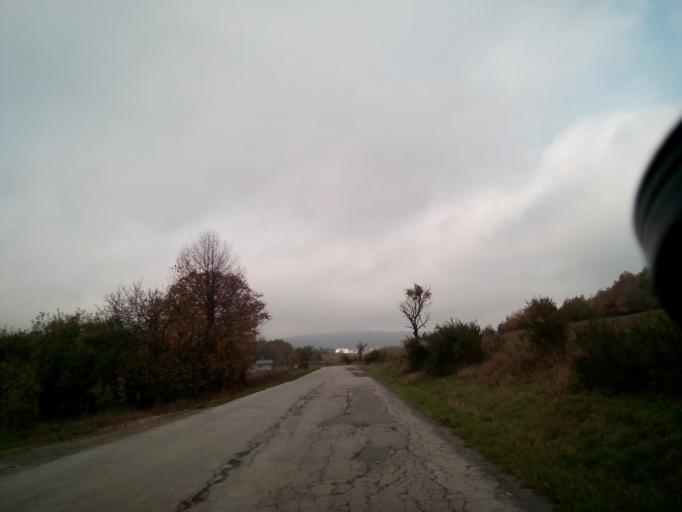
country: SK
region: Kosicky
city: Kosice
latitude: 48.7297
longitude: 21.1352
